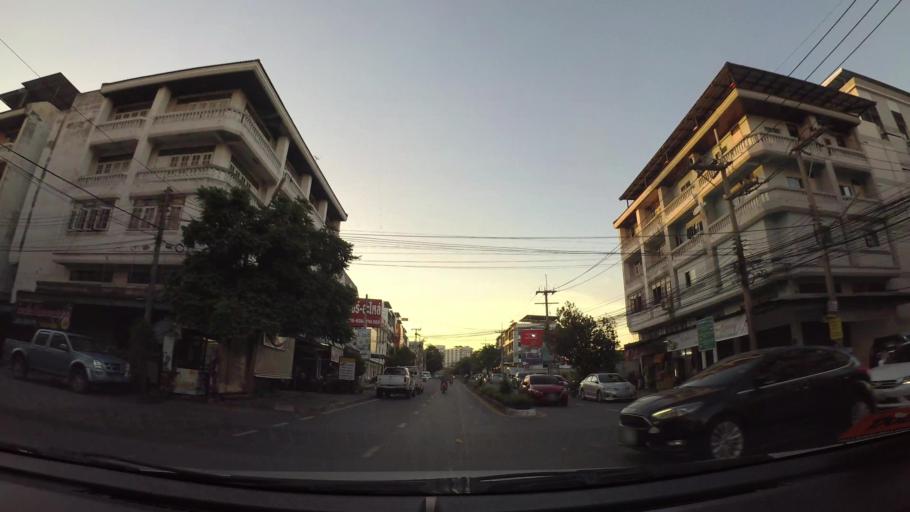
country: TH
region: Chon Buri
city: Bang Lamung
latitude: 13.0903
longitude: 100.9184
